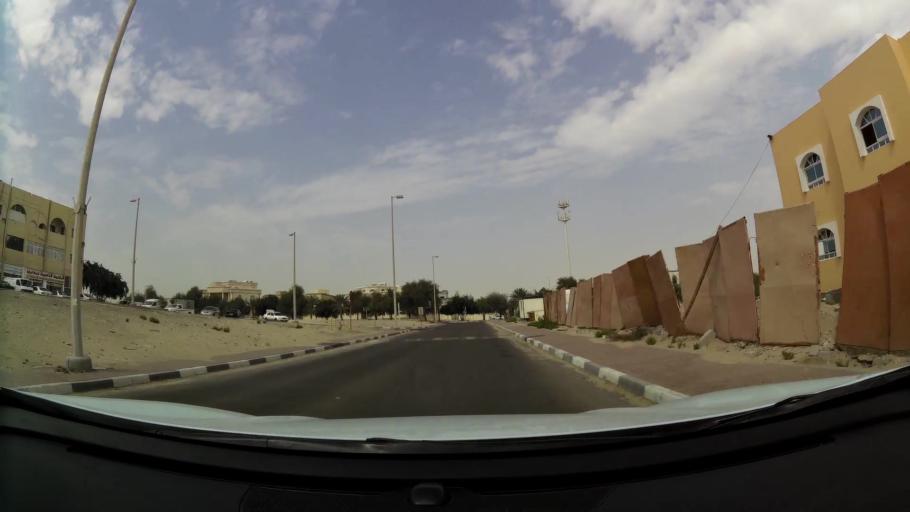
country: AE
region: Abu Dhabi
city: Abu Dhabi
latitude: 24.3050
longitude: 54.6177
